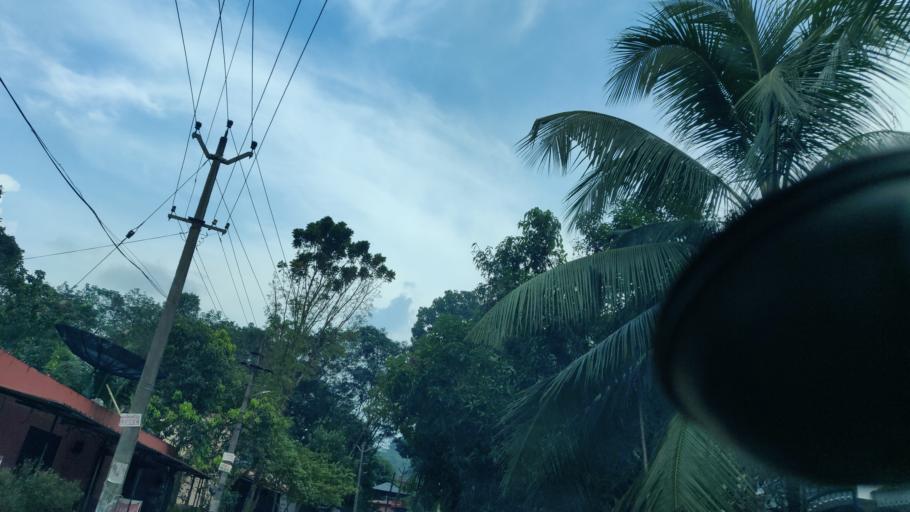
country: IN
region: Kerala
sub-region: Kottayam
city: Lalam
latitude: 9.8390
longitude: 76.7112
